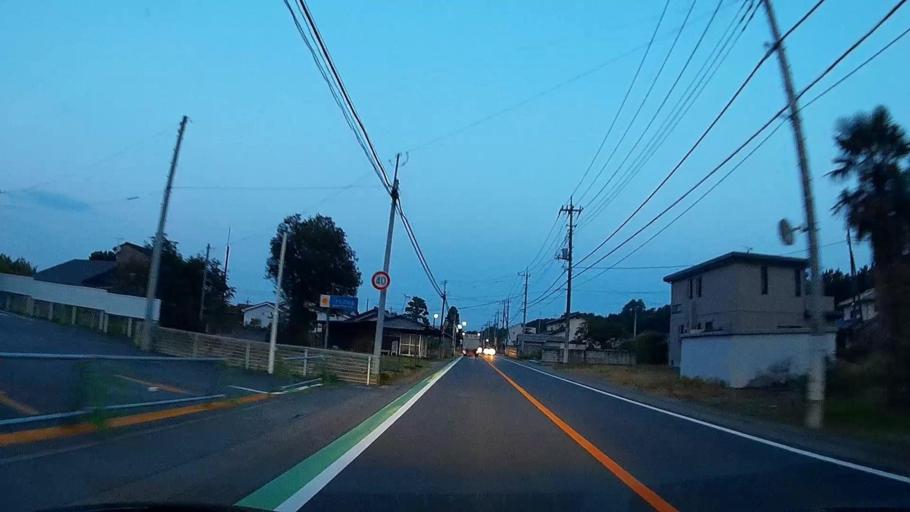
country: JP
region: Gunma
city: Annaka
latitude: 36.3551
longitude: 138.9290
